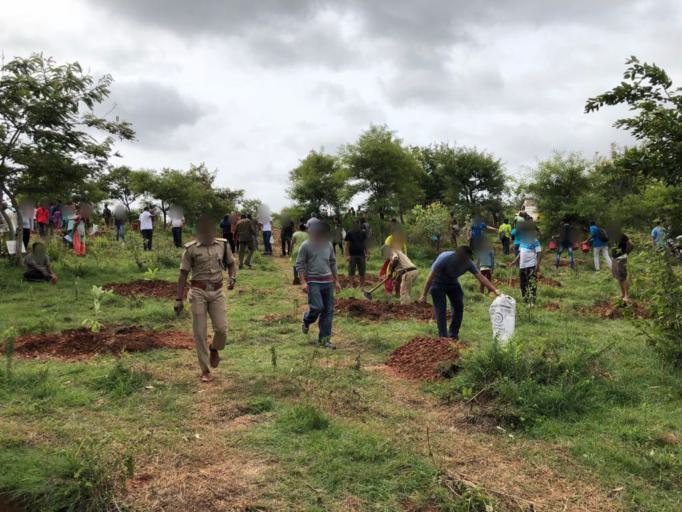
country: IN
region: Karnataka
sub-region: Bangalore Urban
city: Bangalore
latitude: 12.9100
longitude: 77.5021
